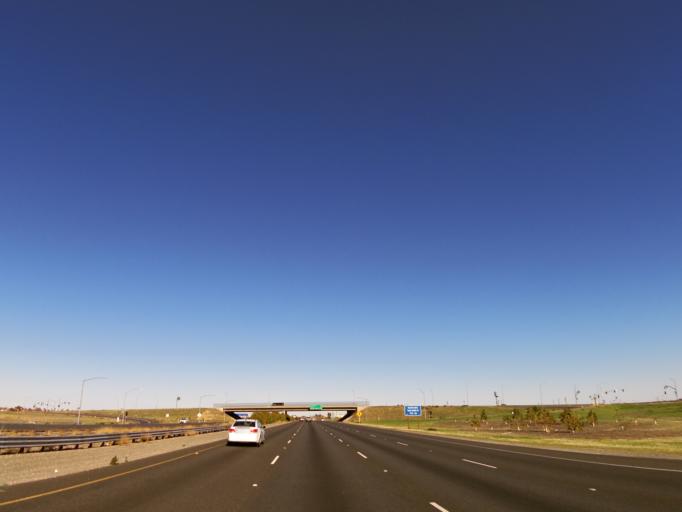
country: US
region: California
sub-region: Yolo County
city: West Sacramento
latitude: 38.6404
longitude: -121.5245
